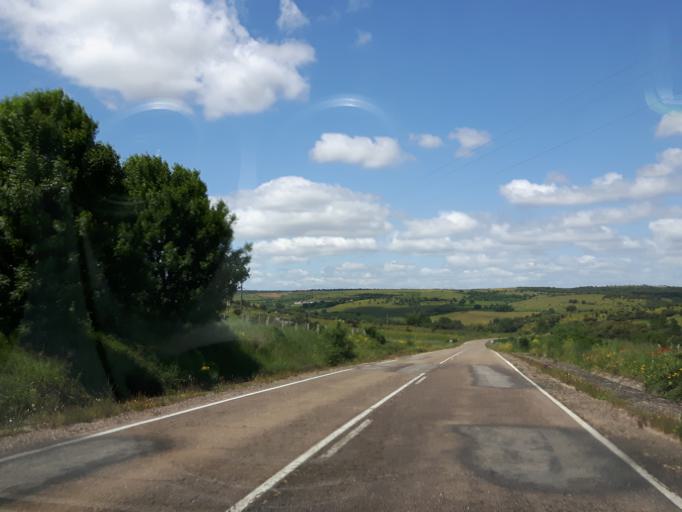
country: ES
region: Castille and Leon
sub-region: Provincia de Salamanca
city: Aldea del Obispo
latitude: 40.7226
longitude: -6.7667
